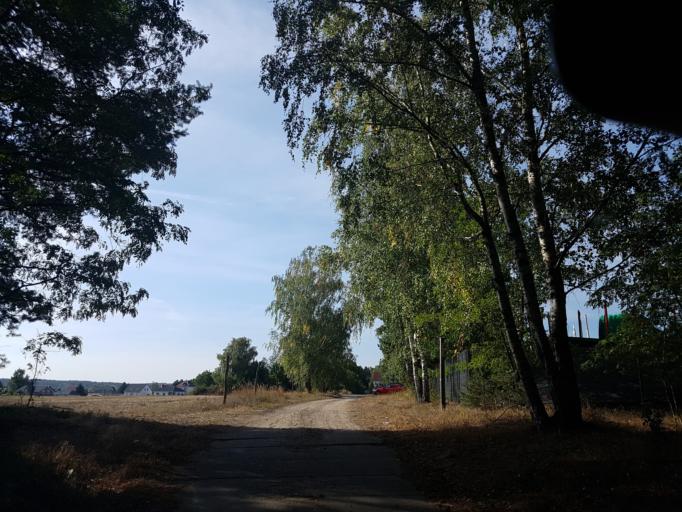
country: DE
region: Brandenburg
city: Belzig
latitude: 52.1494
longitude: 12.5756
